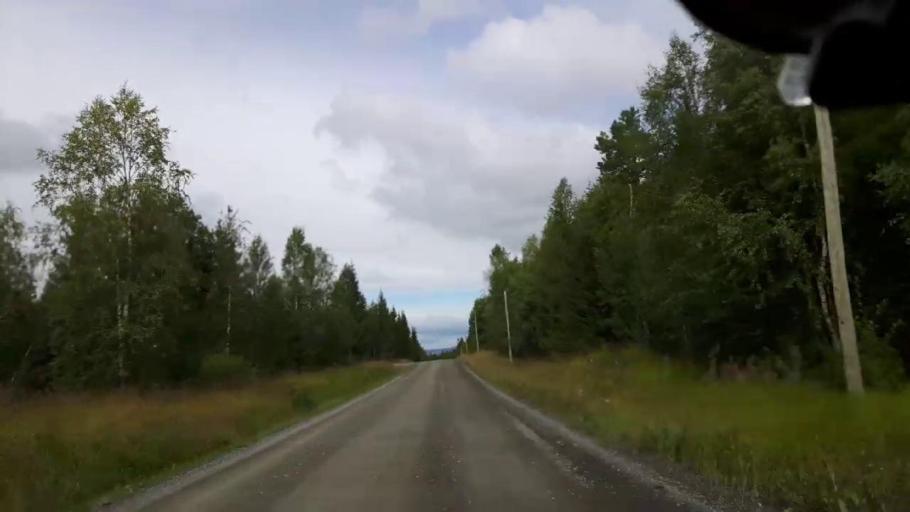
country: SE
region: Jaemtland
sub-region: Krokoms Kommun
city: Krokom
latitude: 63.3850
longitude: 14.1170
